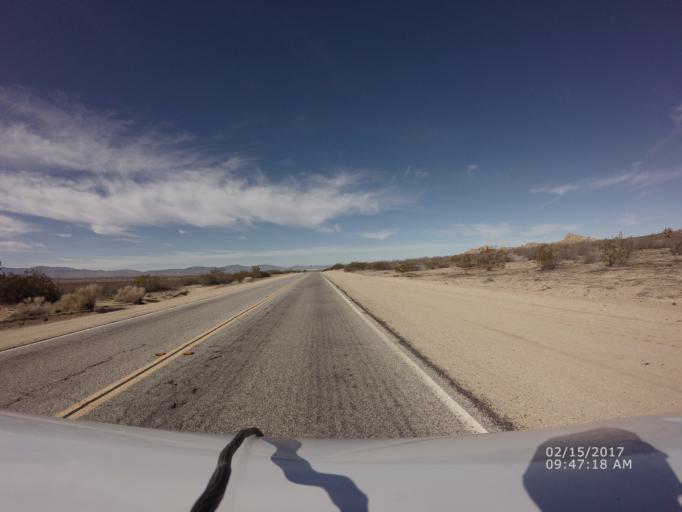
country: US
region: California
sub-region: Los Angeles County
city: Lake Los Angeles
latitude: 34.6166
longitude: -117.9011
